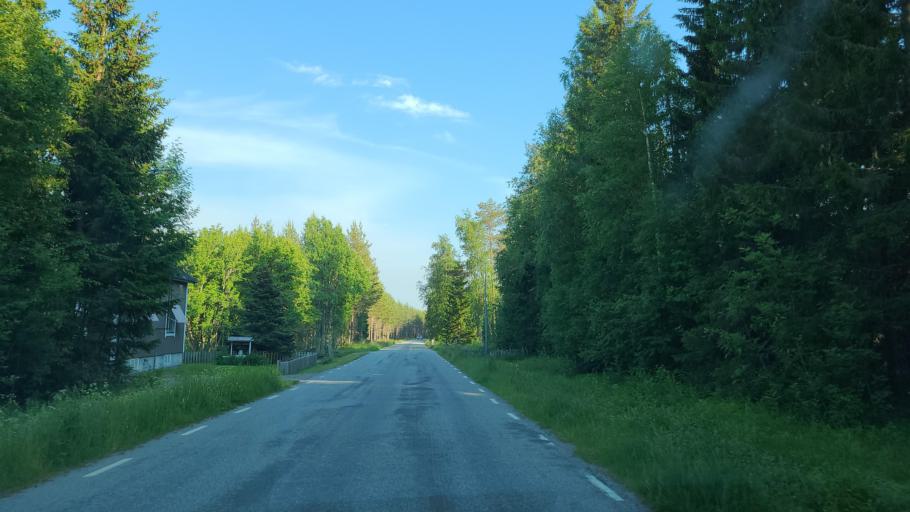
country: SE
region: Vaesterbotten
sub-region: Skelleftea Kommun
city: Burea
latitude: 64.3634
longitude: 21.3309
